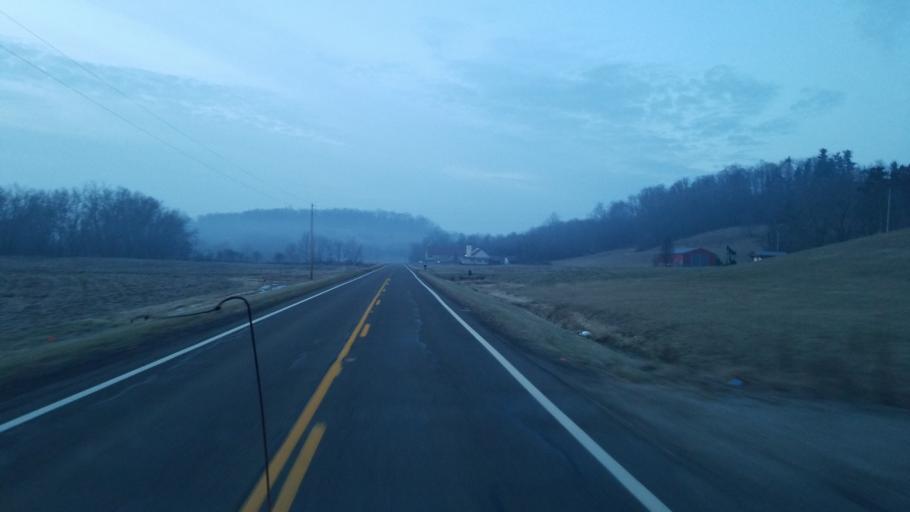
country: US
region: Ohio
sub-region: Coshocton County
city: West Lafayette
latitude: 40.3112
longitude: -81.7490
